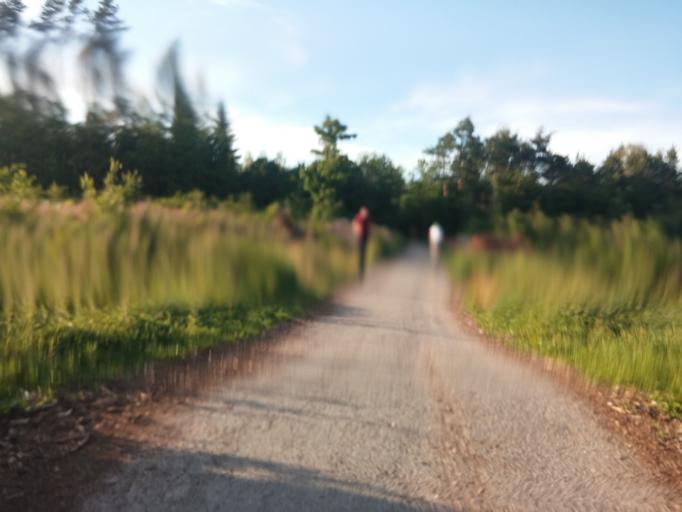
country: DE
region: Bavaria
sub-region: Upper Bavaria
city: Neubiberg
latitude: 48.1021
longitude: 11.6854
